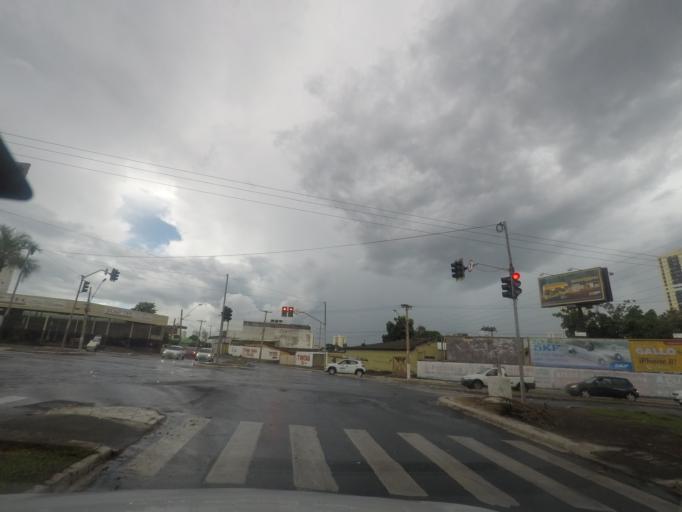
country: BR
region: Goias
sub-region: Goiania
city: Goiania
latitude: -16.6709
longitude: -49.2752
